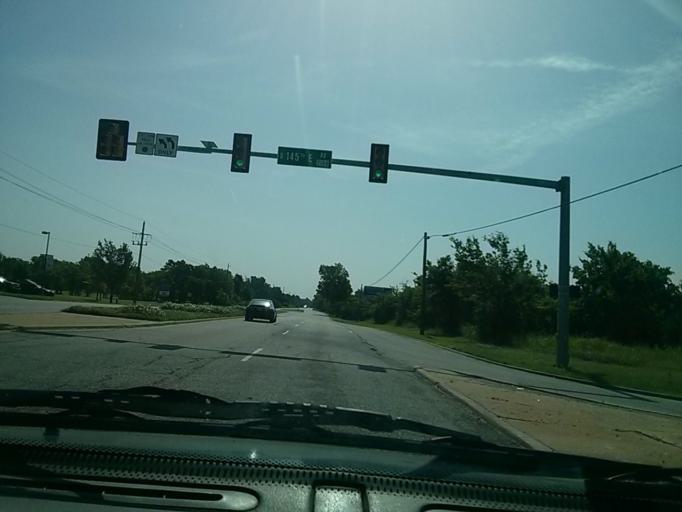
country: US
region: Oklahoma
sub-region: Tulsa County
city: Broken Arrow
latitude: 36.1334
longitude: -95.8155
